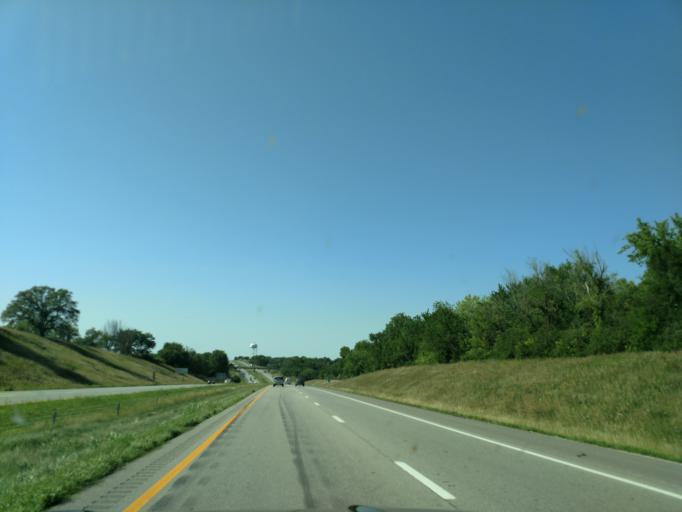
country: US
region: Missouri
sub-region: Andrew County
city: Country Club Village
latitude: 39.7851
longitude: -94.7948
